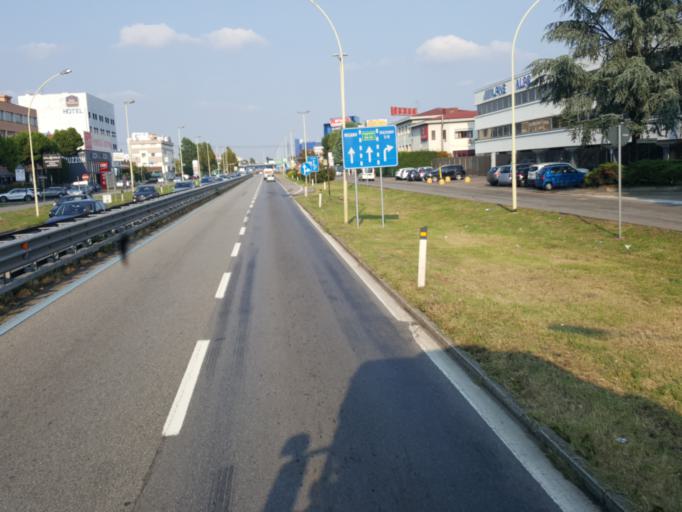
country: IT
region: Lombardy
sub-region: Citta metropolitana di Milano
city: Trezzano sul Naviglio
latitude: 45.4251
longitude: 9.0691
